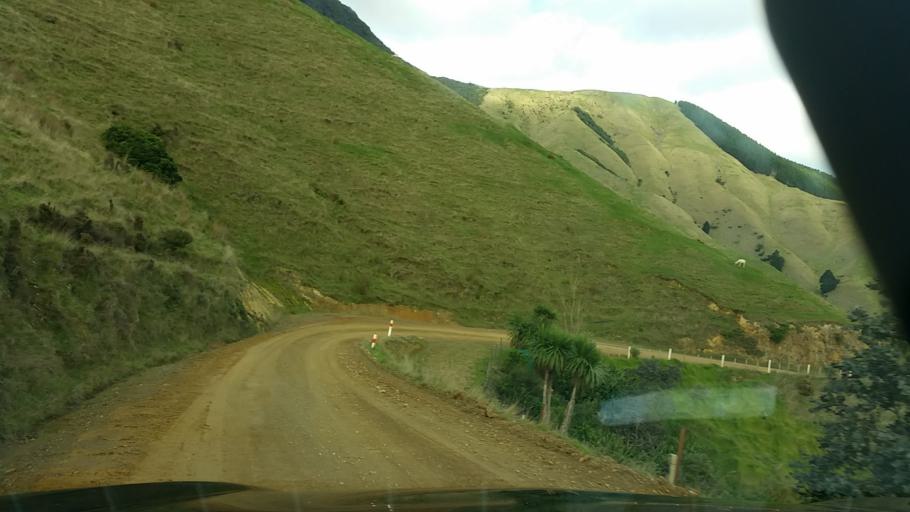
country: NZ
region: Marlborough
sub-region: Marlborough District
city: Picton
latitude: -40.9893
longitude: 173.8317
